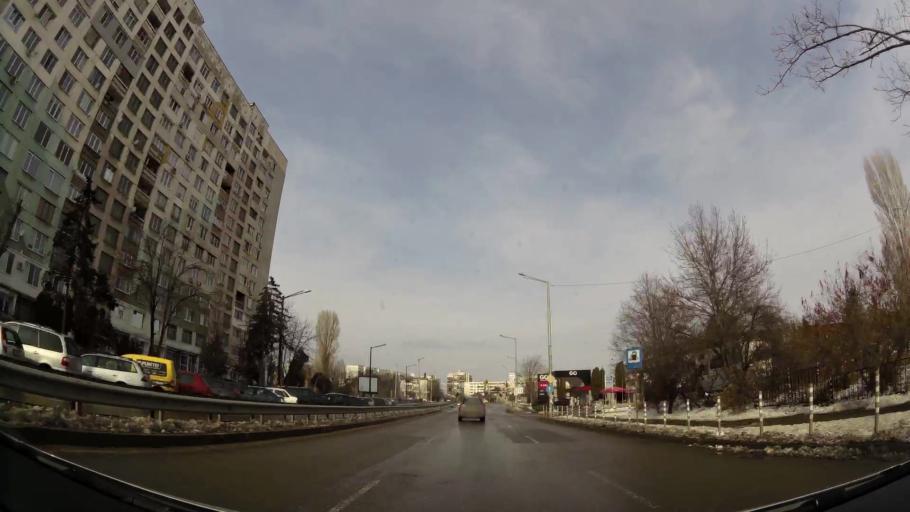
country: BG
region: Sofia-Capital
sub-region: Stolichna Obshtina
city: Sofia
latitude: 42.7037
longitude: 23.3592
